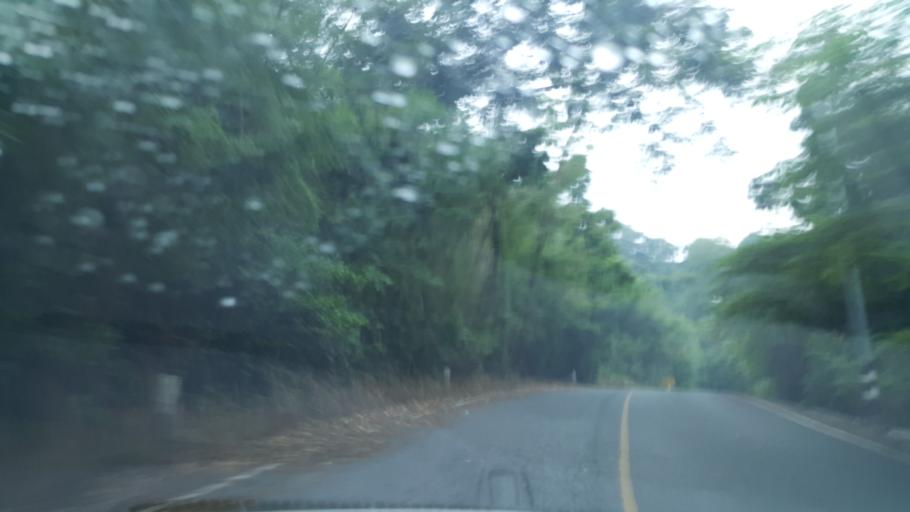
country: TH
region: Chon Buri
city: Ban Bueng
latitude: 13.2397
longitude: 101.0395
